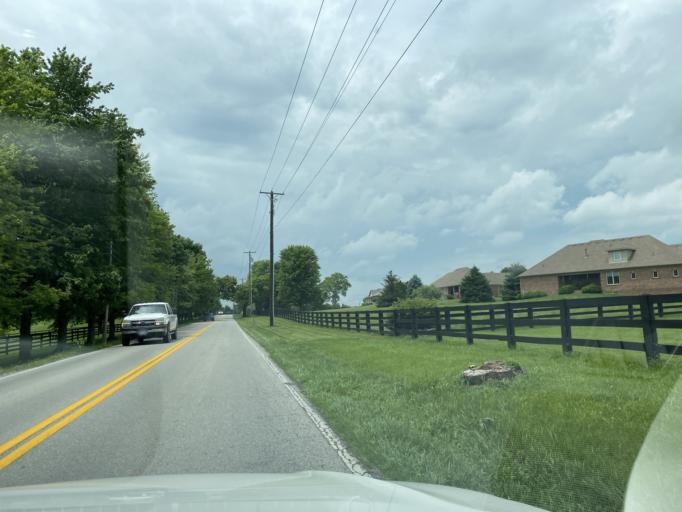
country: US
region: Kentucky
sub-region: Scott County
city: Georgetown
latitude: 38.2193
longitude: -84.4837
